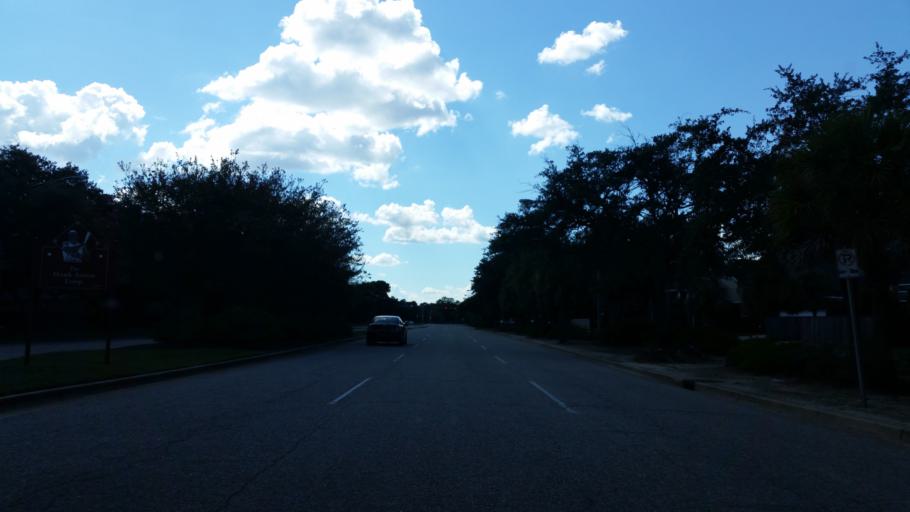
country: US
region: Alabama
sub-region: Mobile County
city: Mobile
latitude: 30.6836
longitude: -88.0458
